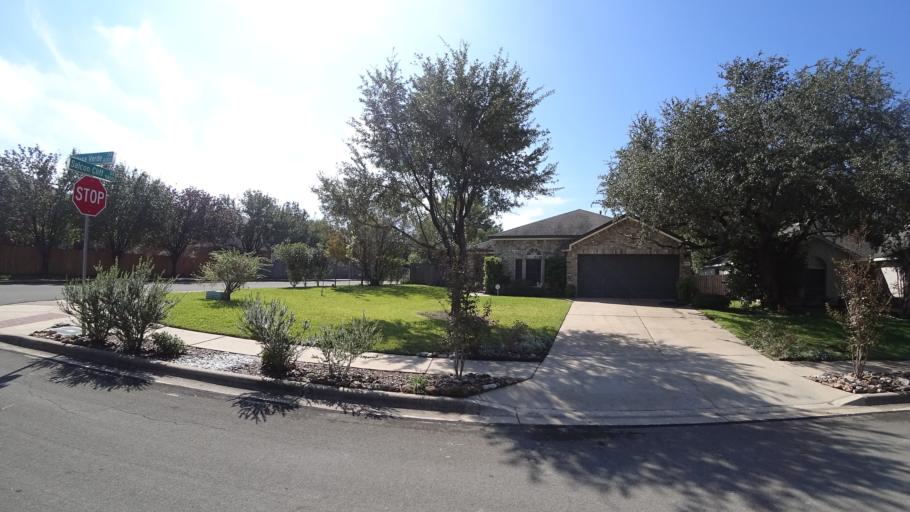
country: US
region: Texas
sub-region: Travis County
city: Shady Hollow
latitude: 30.2089
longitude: -97.8735
